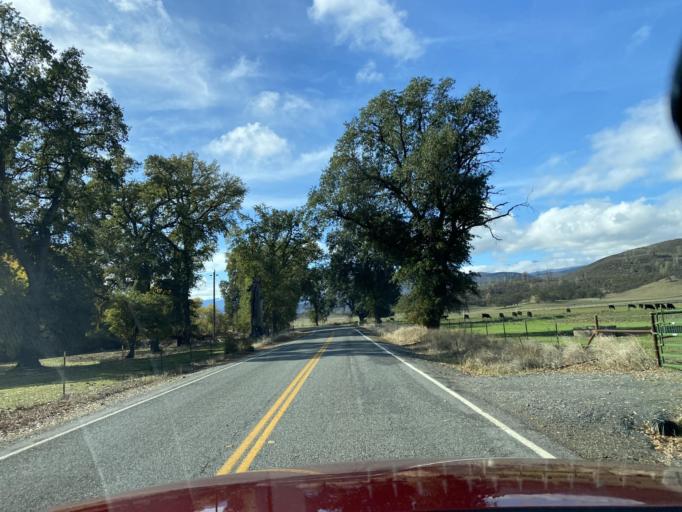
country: US
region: California
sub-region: Glenn County
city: Willows
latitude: 39.4142
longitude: -122.5430
